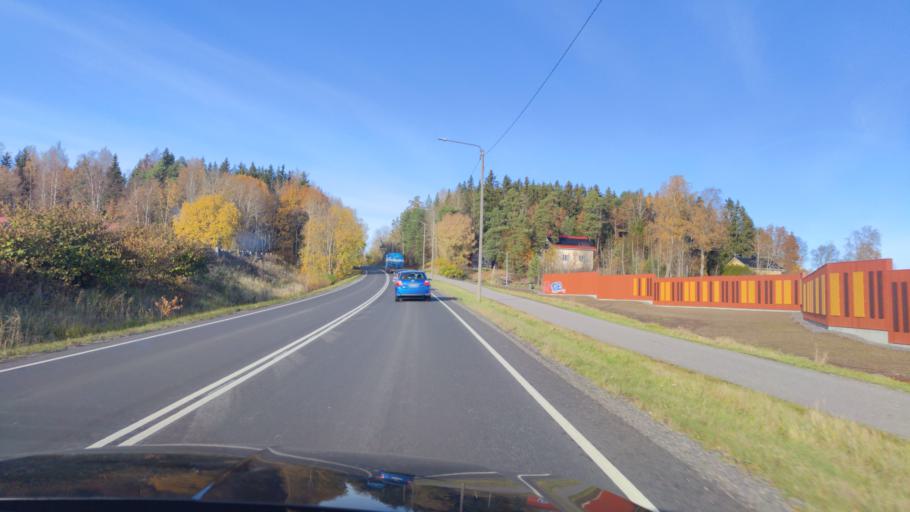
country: FI
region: Varsinais-Suomi
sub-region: Turku
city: Kaarina
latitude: 60.4386
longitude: 22.3837
